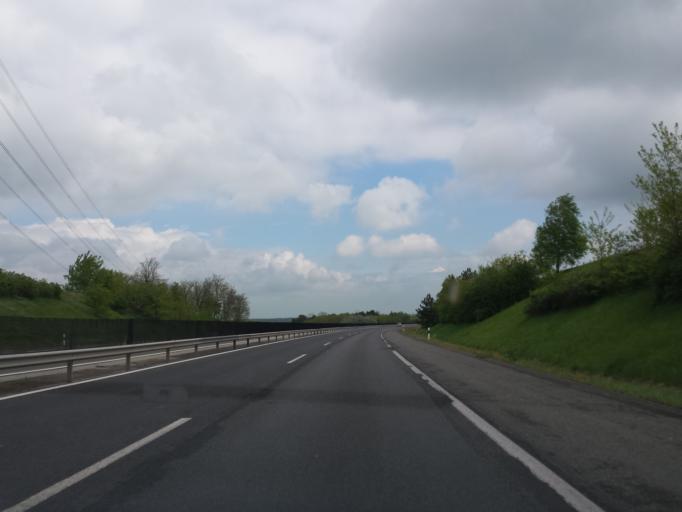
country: HU
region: Gyor-Moson-Sopron
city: Per
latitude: 47.6840
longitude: 17.7964
